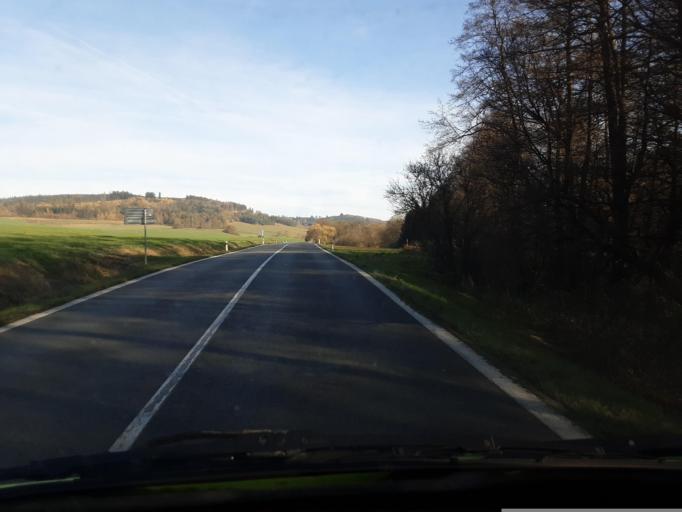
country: CZ
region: Plzensky
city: Klatovy
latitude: 49.3601
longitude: 13.3697
